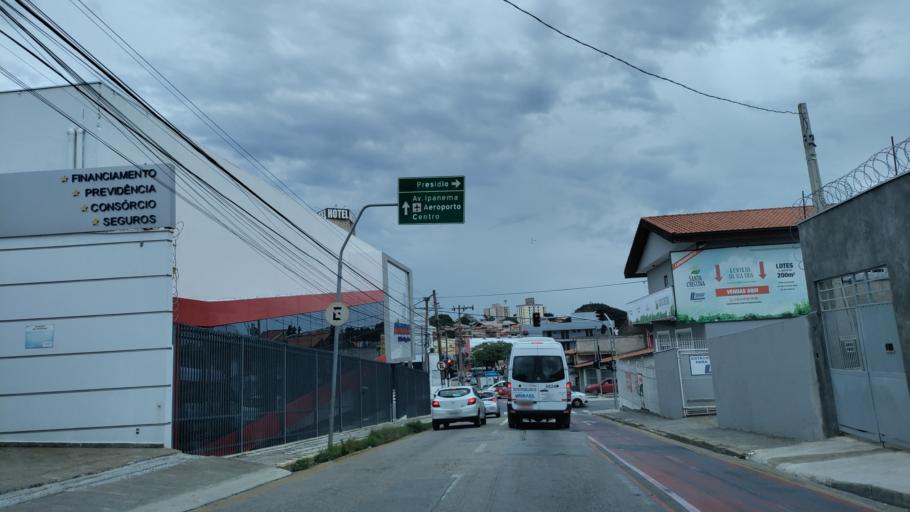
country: BR
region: Sao Paulo
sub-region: Sorocaba
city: Sorocaba
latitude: -23.4824
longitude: -47.4720
